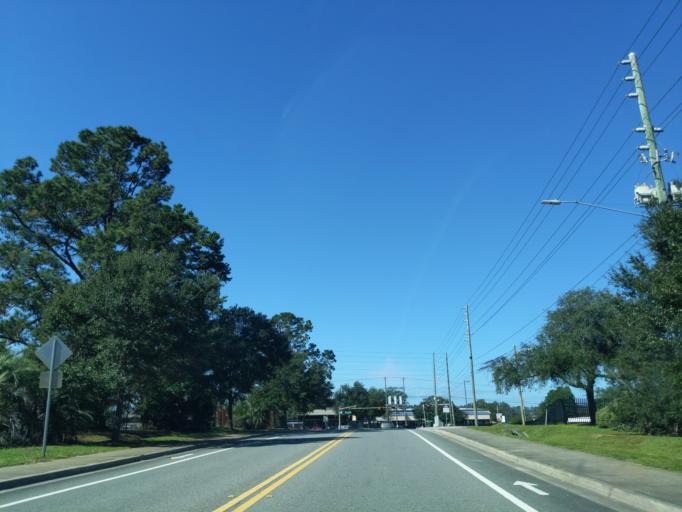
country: US
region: Florida
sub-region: Leon County
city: Tallahassee
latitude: 30.4515
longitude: -84.2251
